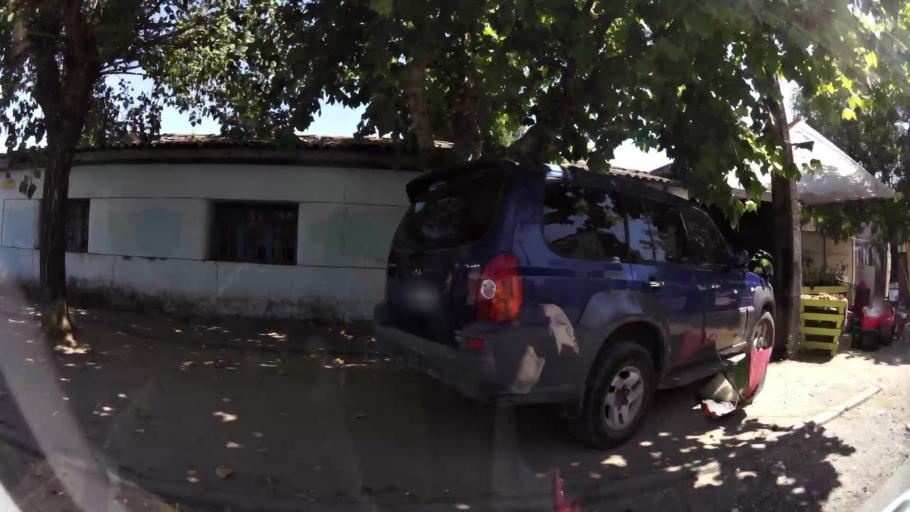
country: CL
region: Maule
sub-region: Provincia de Talca
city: Talca
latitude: -35.4144
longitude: -71.6519
